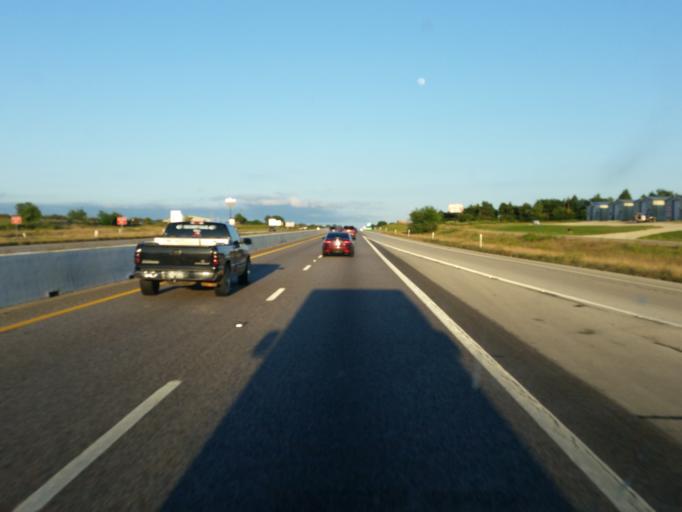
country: US
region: Texas
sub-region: Van Zandt County
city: Wills Point
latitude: 32.6165
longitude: -95.9751
